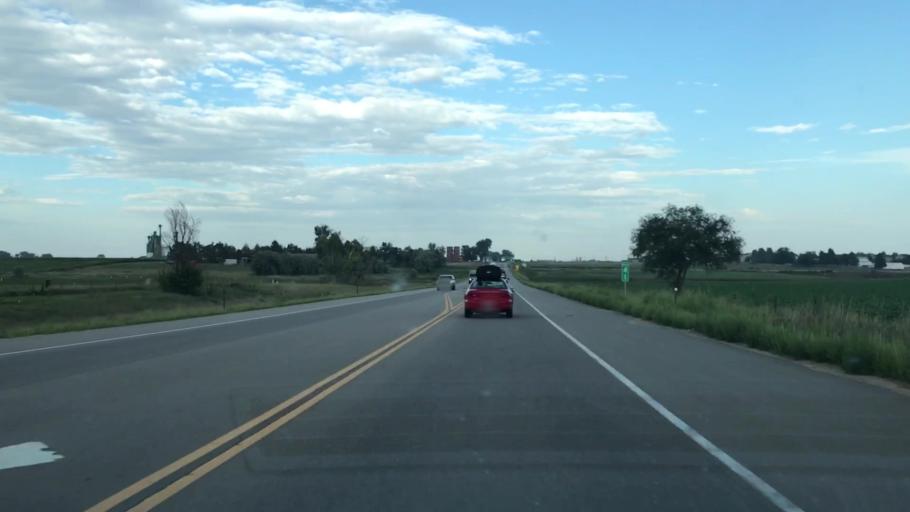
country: US
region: Colorado
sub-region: Weld County
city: Mead
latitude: 40.2039
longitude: -105.0162
